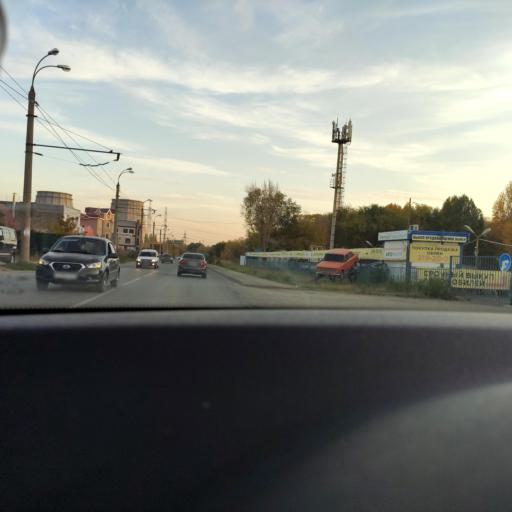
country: RU
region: Samara
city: Petra-Dubrava
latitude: 53.2557
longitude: 50.2656
